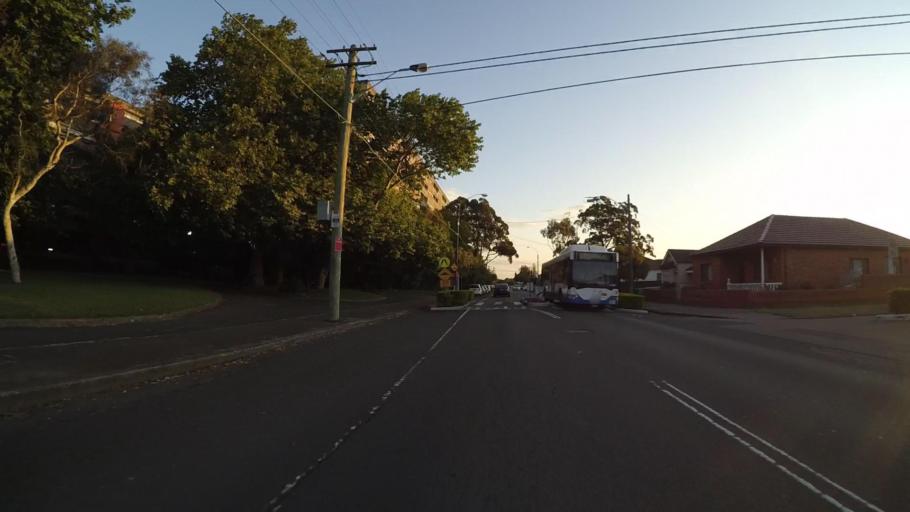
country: AU
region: New South Wales
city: Alexandria
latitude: -33.9249
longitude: 151.2066
